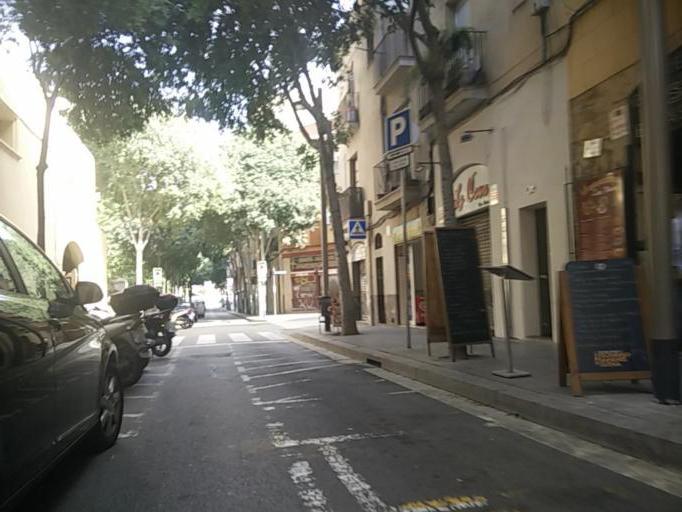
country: ES
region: Catalonia
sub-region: Provincia de Barcelona
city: Sants-Montjuic
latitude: 41.3777
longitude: 2.1434
